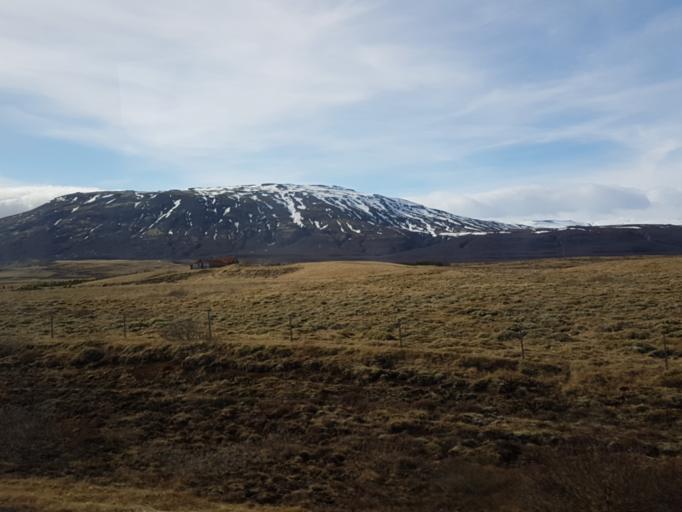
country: IS
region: South
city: Selfoss
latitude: 64.2425
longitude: -20.5047
